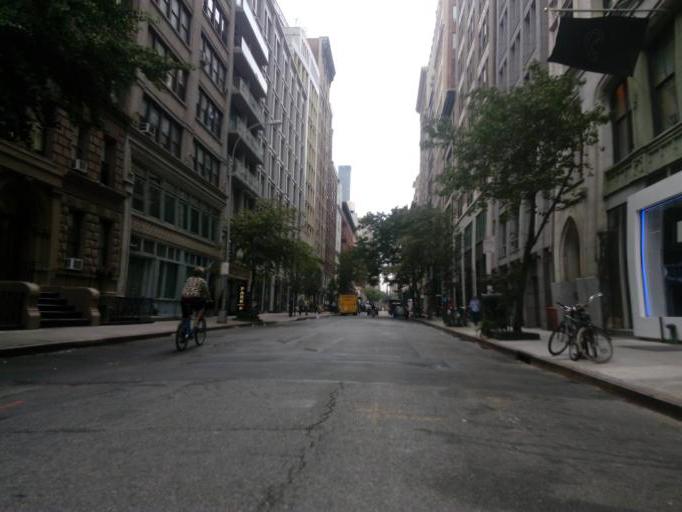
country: US
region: New York
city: New York City
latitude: 40.7428
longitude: -73.9956
